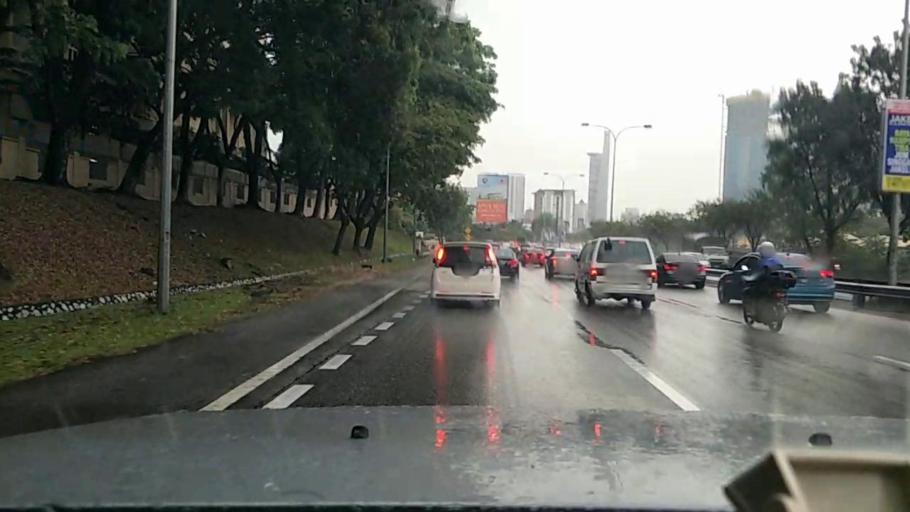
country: MY
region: Kuala Lumpur
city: Kuala Lumpur
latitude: 3.1122
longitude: 101.6855
